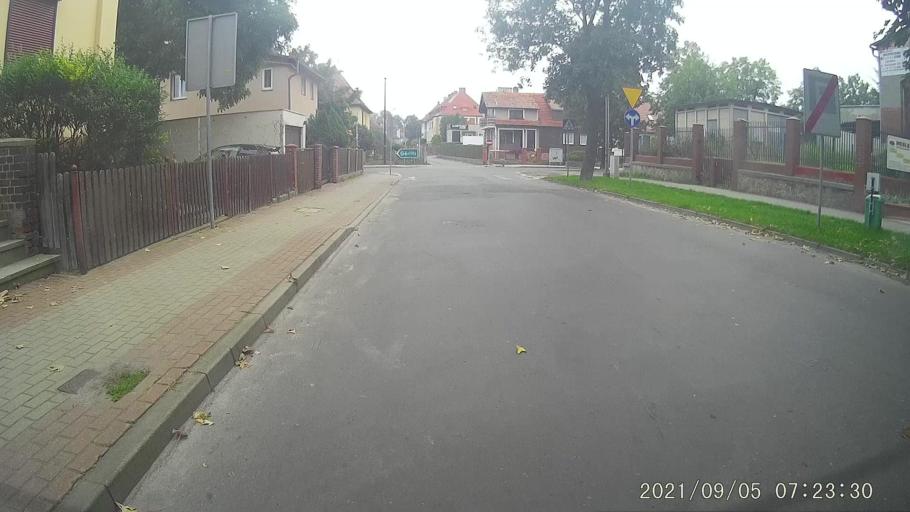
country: DE
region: Saxony
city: Boxberg
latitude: 51.4369
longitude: 14.6020
